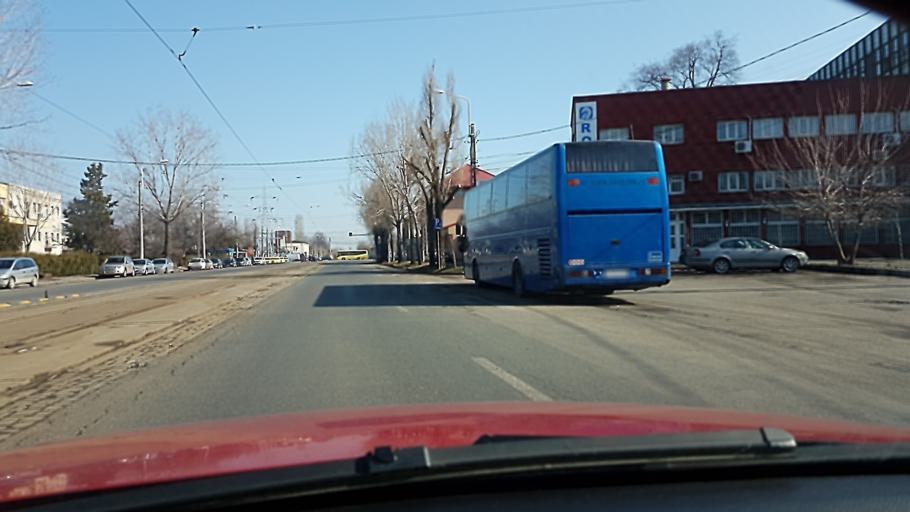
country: RO
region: Ilfov
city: Dobroesti
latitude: 44.4342
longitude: 26.1836
